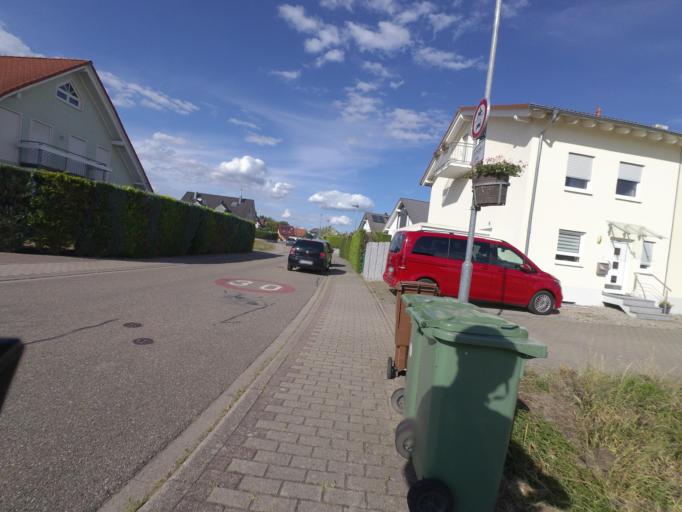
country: DE
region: Baden-Wuerttemberg
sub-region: Karlsruhe Region
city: Sinzheim
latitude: 48.7728
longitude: 8.1663
